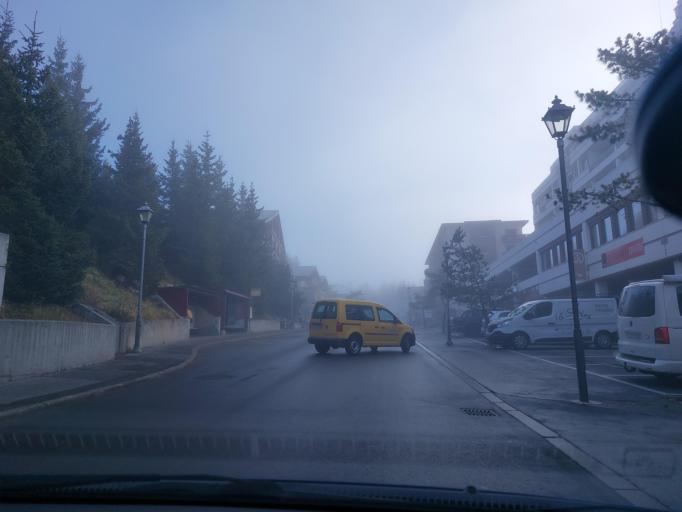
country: CH
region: Valais
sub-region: Sierre District
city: Montana
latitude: 46.3073
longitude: 7.4663
